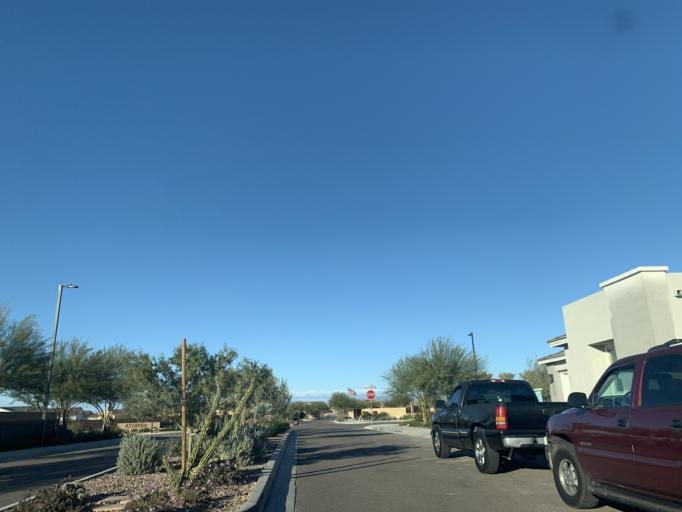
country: US
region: Arizona
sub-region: Maricopa County
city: Cave Creek
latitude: 33.6884
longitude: -112.0156
